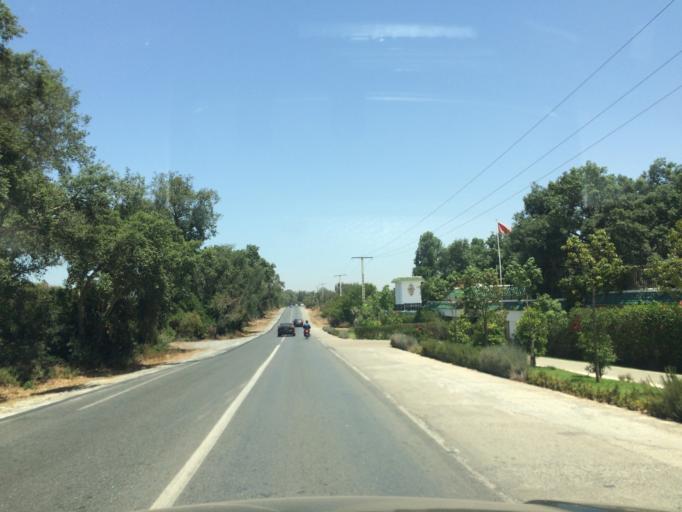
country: MA
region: Rabat-Sale-Zemmour-Zaer
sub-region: Skhirate-Temara
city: Temara
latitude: 33.8990
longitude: -6.8286
